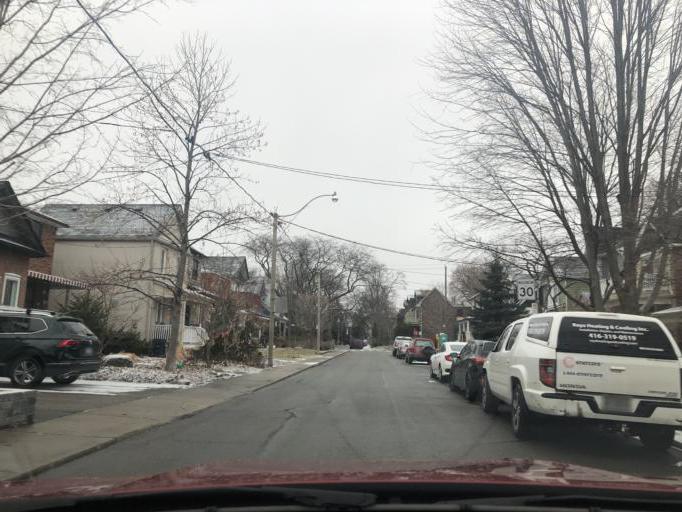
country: CA
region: Ontario
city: Toronto
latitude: 43.6761
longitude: -79.3375
